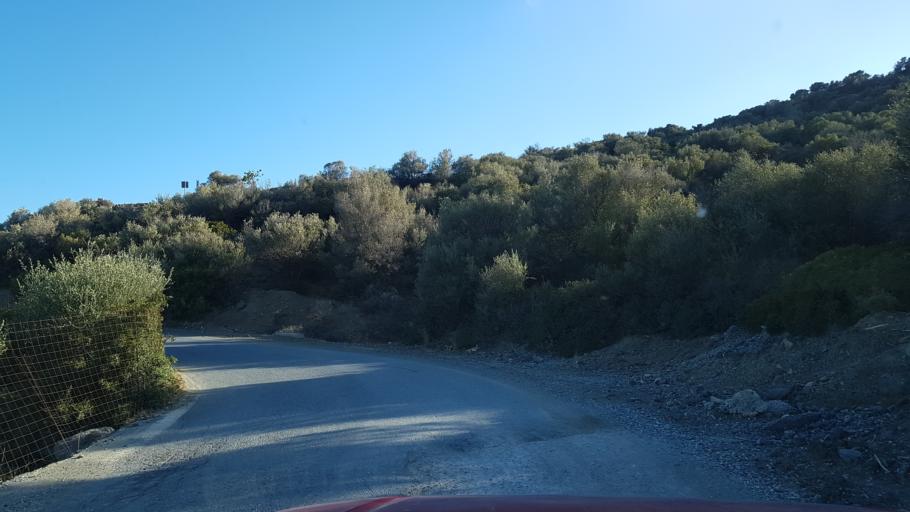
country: GR
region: Crete
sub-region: Nomos Irakleiou
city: Moires
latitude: 34.9351
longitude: 24.8050
